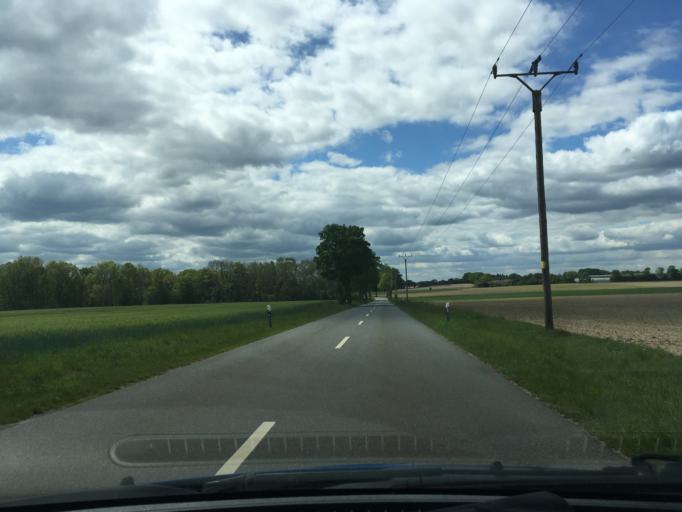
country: DE
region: Lower Saxony
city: Suderburg
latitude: 52.9182
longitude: 10.5028
